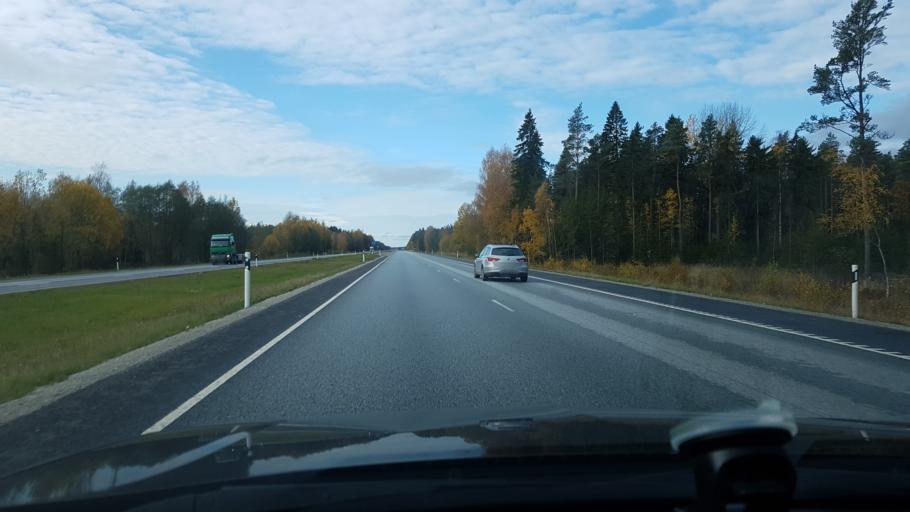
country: EE
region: Harju
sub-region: Loksa linn
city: Loksa
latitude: 59.4633
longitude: 25.6812
